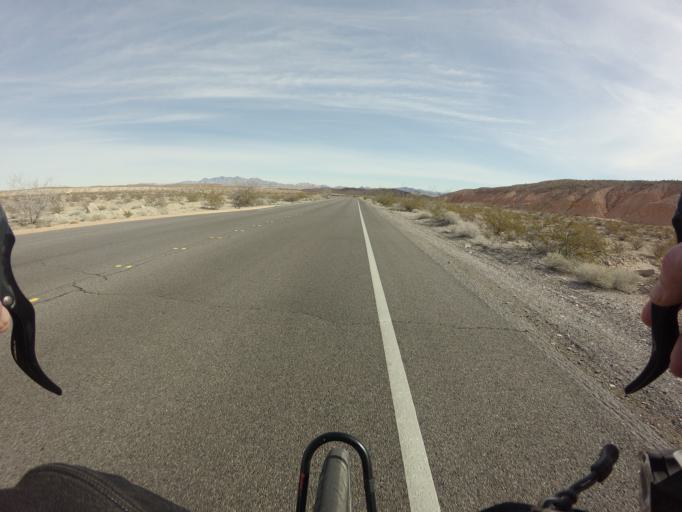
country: US
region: Nevada
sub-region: Clark County
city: Henderson
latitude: 36.1362
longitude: -114.9047
